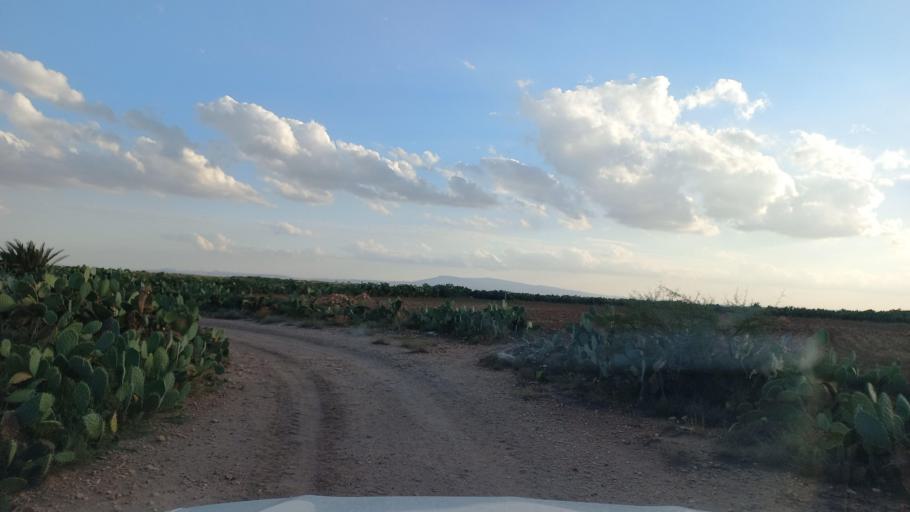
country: TN
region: Al Qasrayn
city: Sbiba
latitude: 35.3763
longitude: 9.0513
